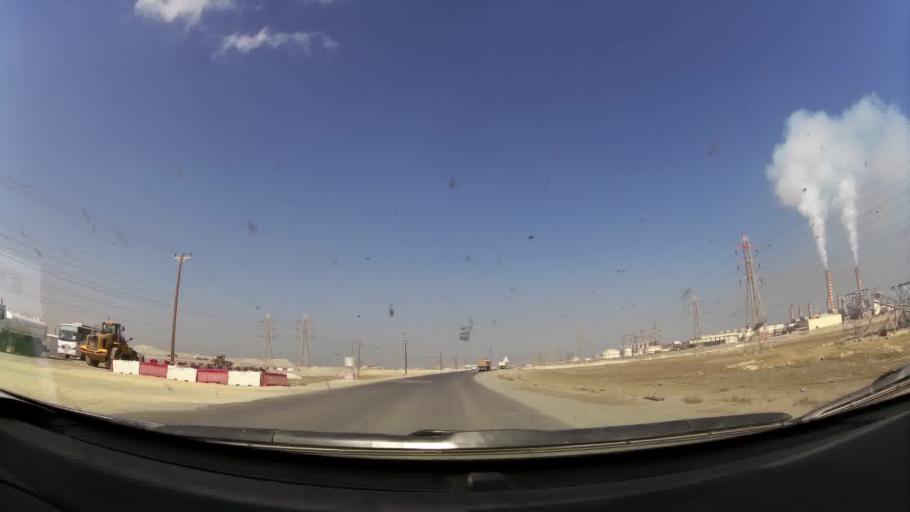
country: SA
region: Eastern Province
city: Al Khafji
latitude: 28.6996
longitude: 48.3584
